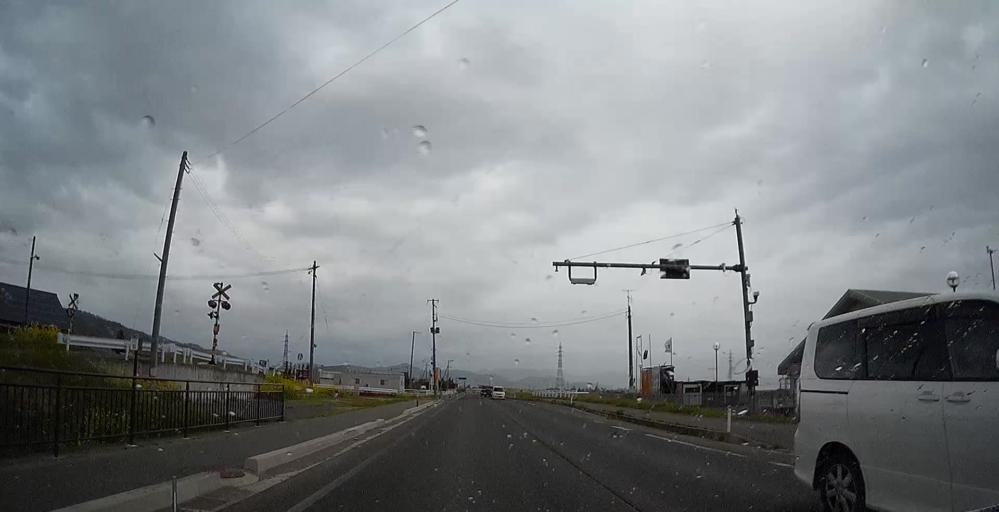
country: JP
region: Yamagata
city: Nagai
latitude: 38.0522
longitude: 140.0903
